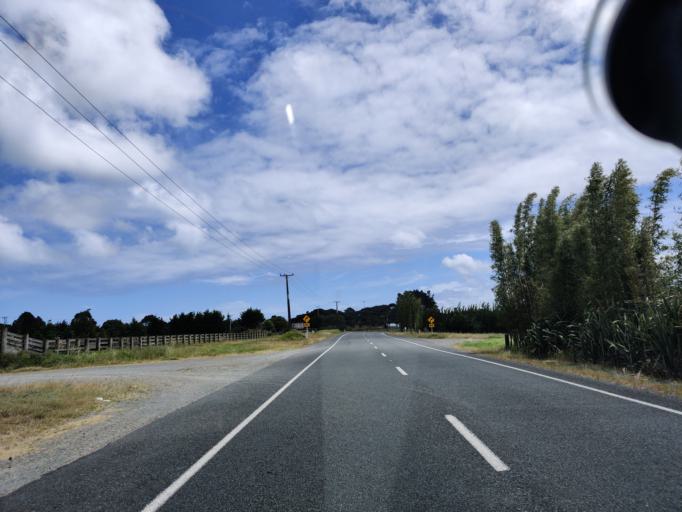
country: NZ
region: Northland
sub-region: Far North District
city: Kaitaia
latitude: -34.8718
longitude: 173.1498
